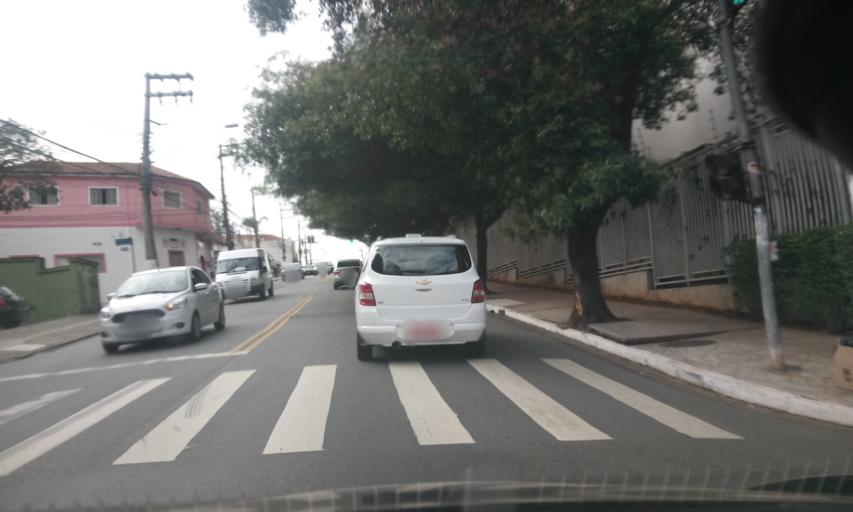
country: BR
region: Sao Paulo
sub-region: Sao Paulo
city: Sao Paulo
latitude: -23.6026
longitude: -46.6177
